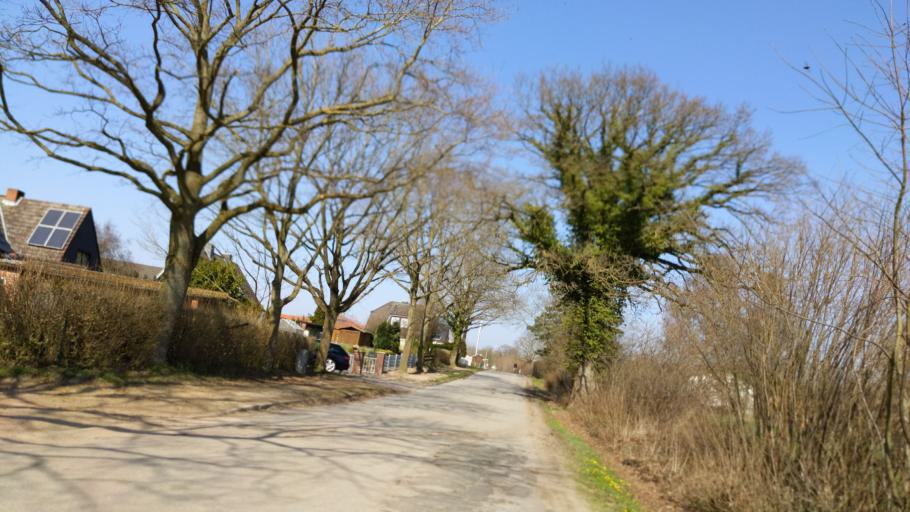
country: DE
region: Schleswig-Holstein
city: Susel
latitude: 54.1003
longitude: 10.7123
